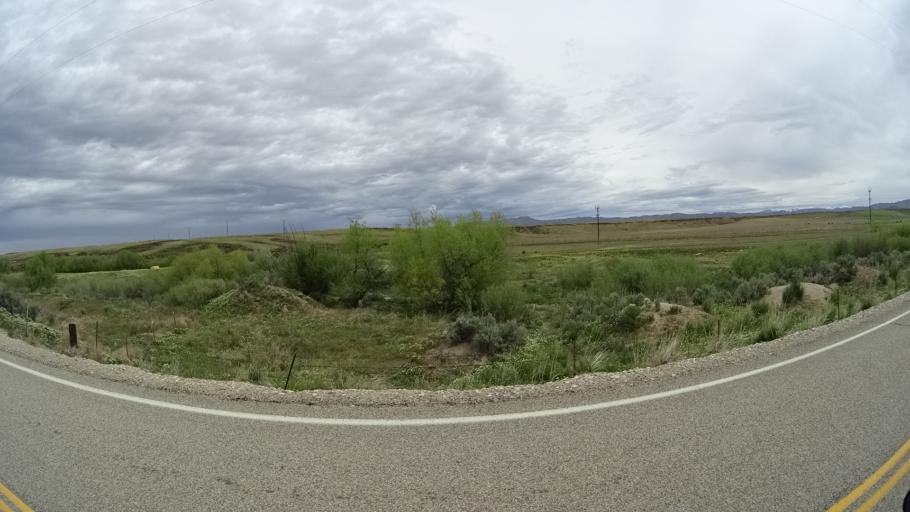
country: US
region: Idaho
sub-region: Ada County
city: Boise
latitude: 43.3888
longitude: -115.9872
